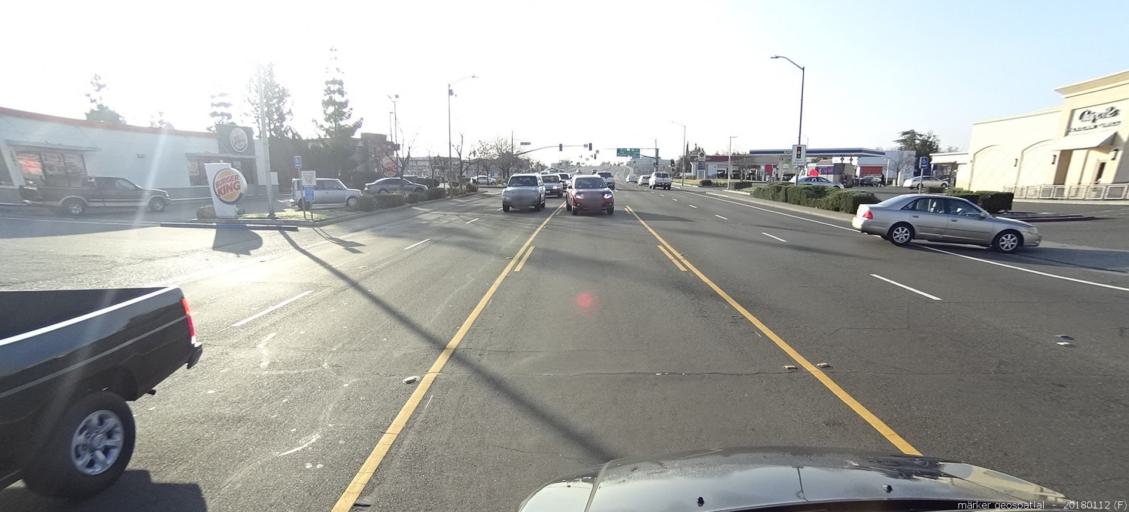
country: US
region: California
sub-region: Sacramento County
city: Rancho Cordova
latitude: 38.5947
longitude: -121.2881
